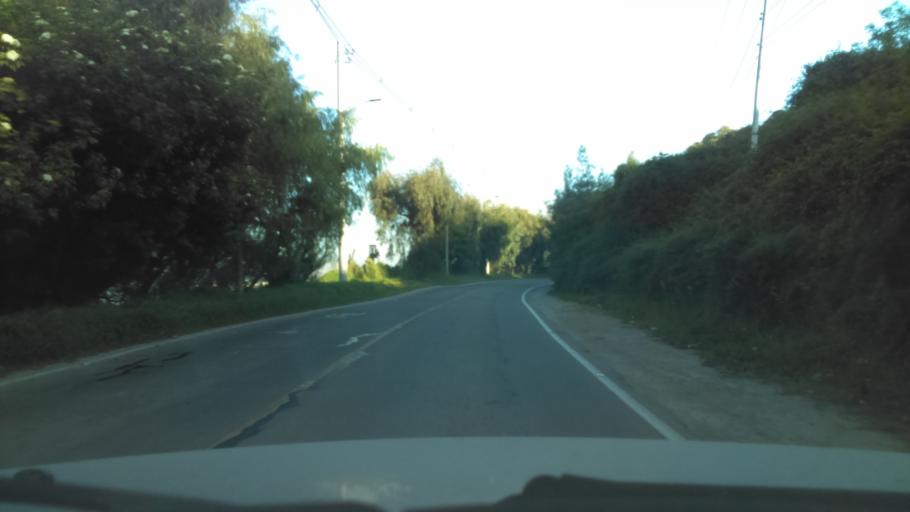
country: CO
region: Cundinamarca
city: Sibate
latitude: 4.5167
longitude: -74.2448
